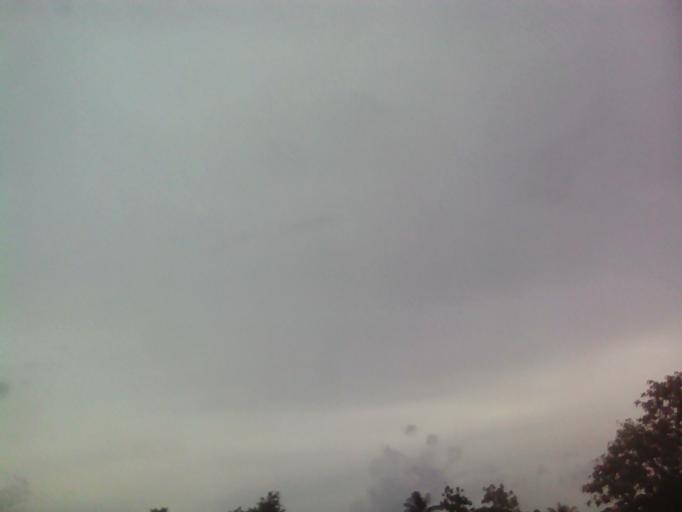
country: MY
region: Penang
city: Perai
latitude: 5.3967
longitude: 100.4184
